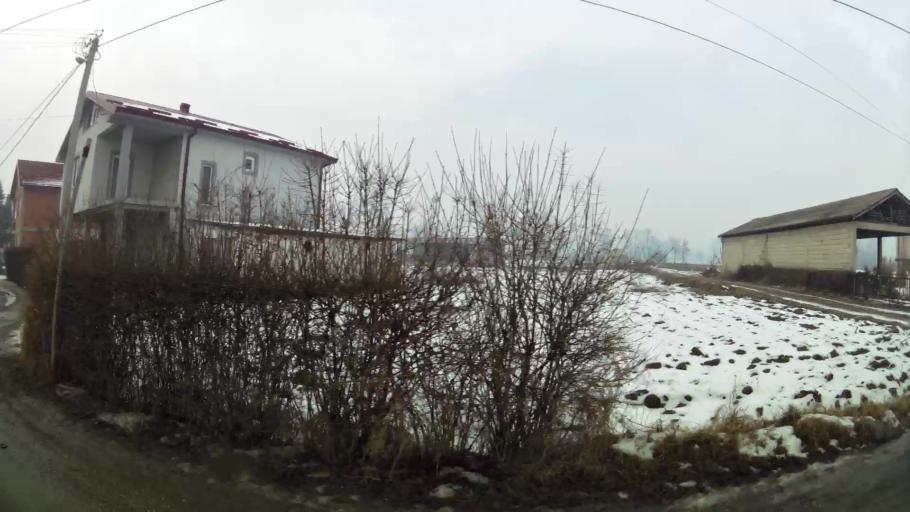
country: MK
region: Ilinden
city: Jurumleri
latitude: 41.9714
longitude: 21.5560
